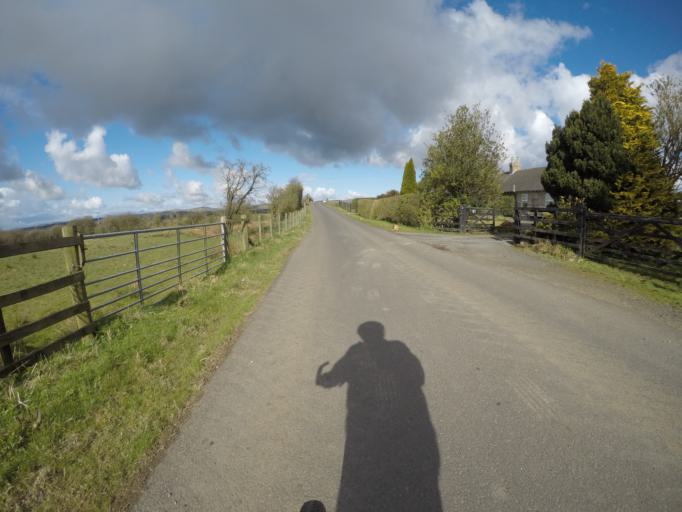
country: GB
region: Scotland
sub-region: North Ayrshire
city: Kilwinning
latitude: 55.6874
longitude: -4.6608
